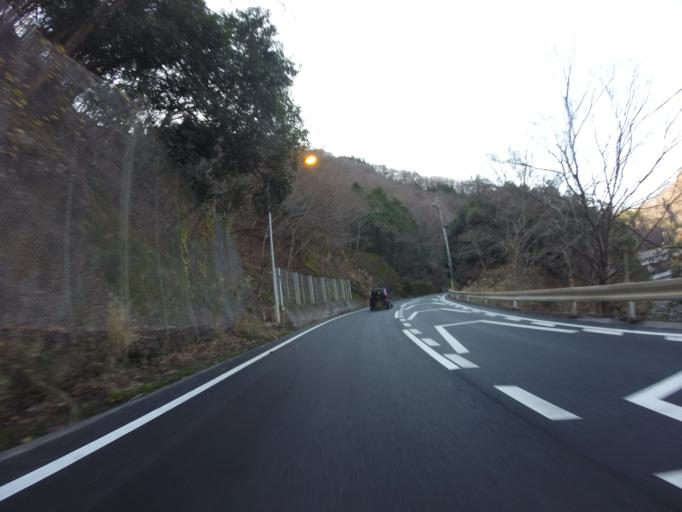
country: JP
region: Yamanashi
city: Ryuo
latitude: 35.4254
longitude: 138.4098
